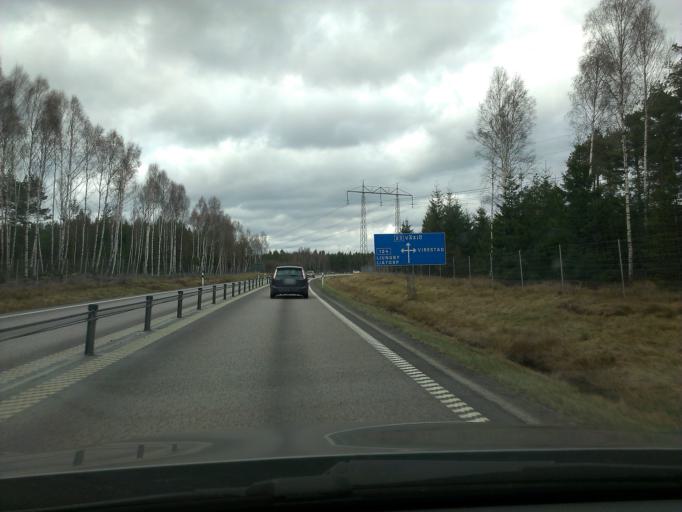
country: SE
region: Kronoberg
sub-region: Almhults Kommun
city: AElmhult
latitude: 56.6574
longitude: 14.2884
